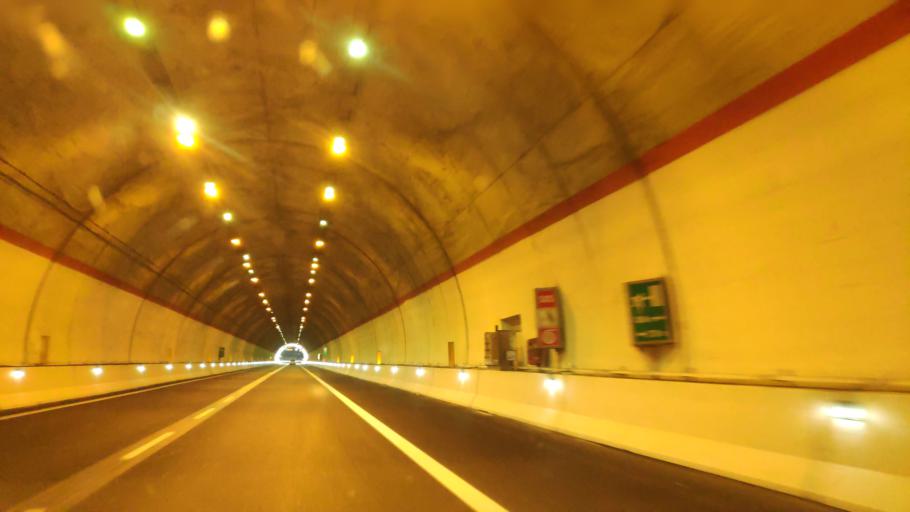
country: IT
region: Calabria
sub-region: Provincia di Reggio Calabria
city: Bagnara Calabra
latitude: 38.2636
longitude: 15.7818
